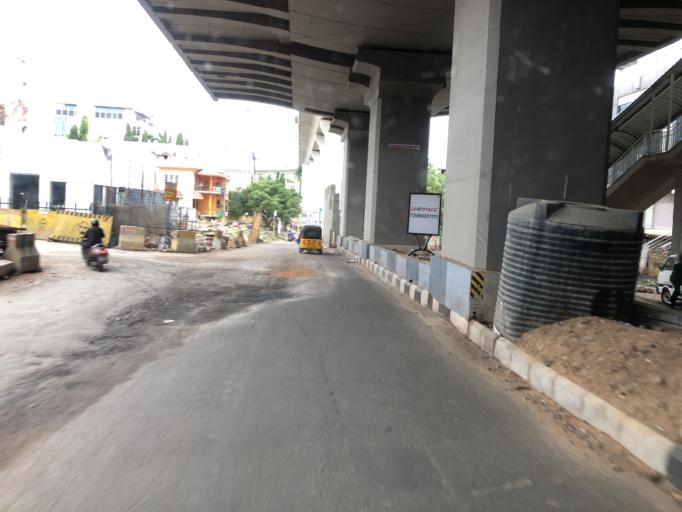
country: IN
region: Telangana
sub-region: Rangareddi
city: Kukatpalli
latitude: 17.4301
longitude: 78.4229
